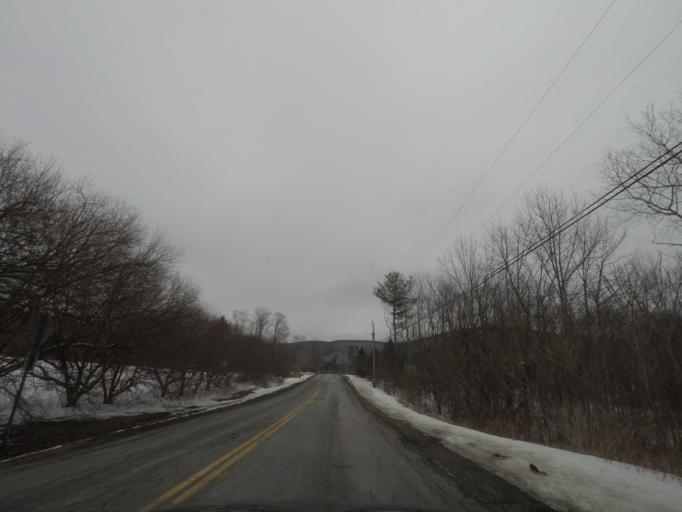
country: US
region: Massachusetts
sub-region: Berkshire County
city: Lanesborough
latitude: 42.5984
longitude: -73.3641
